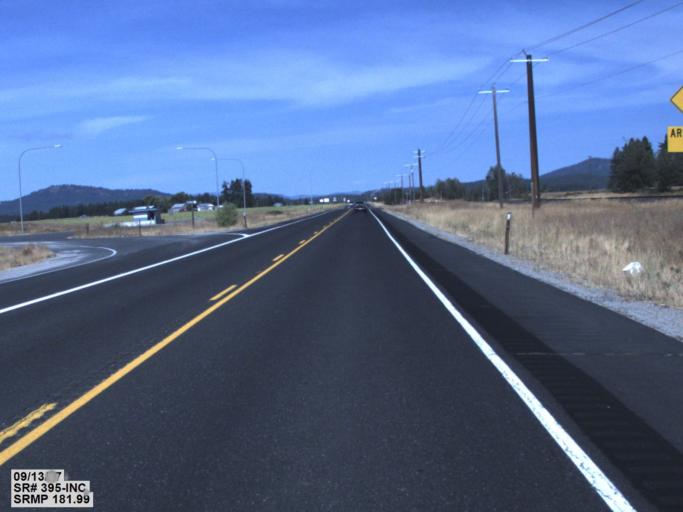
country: US
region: Washington
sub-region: Spokane County
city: Deer Park
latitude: 47.9700
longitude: -117.5109
